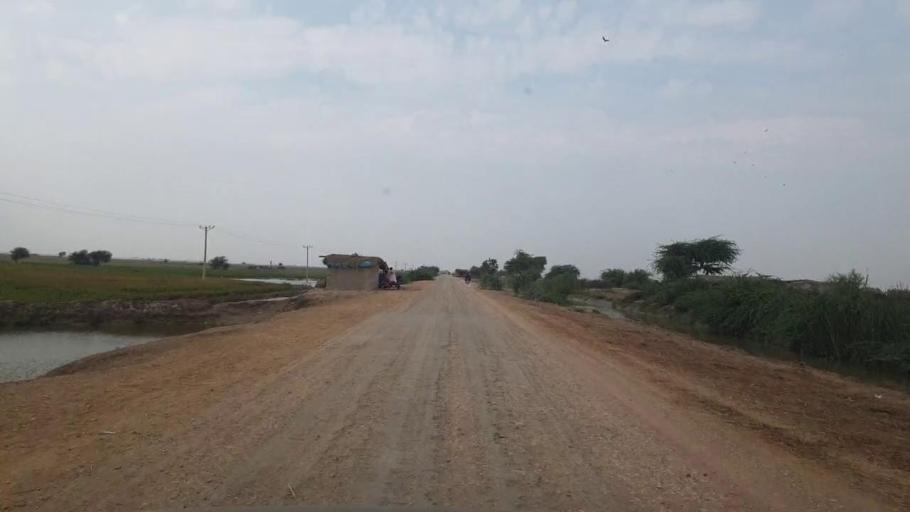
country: PK
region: Sindh
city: Kario
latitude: 24.6088
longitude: 68.5943
